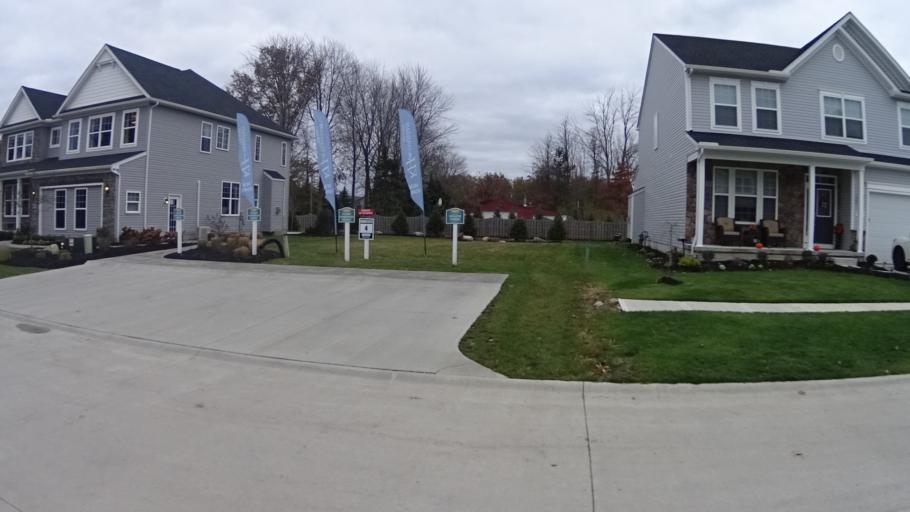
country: US
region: Ohio
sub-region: Lorain County
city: Avon Lake
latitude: 41.4848
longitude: -82.0205
